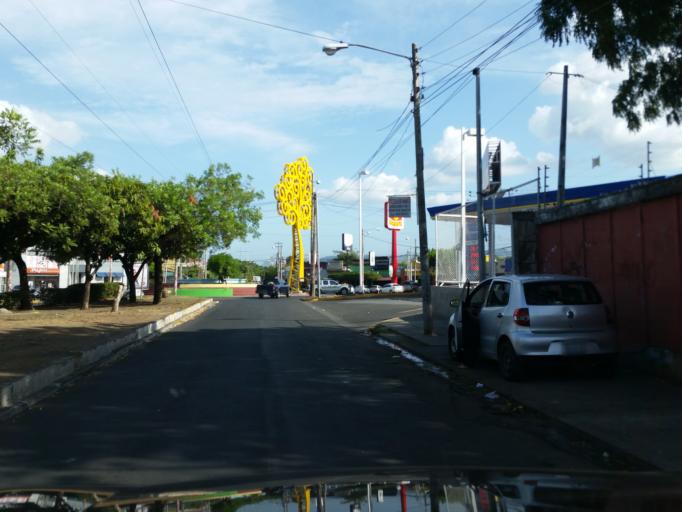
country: NI
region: Managua
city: Managua
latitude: 12.1467
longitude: -86.2341
